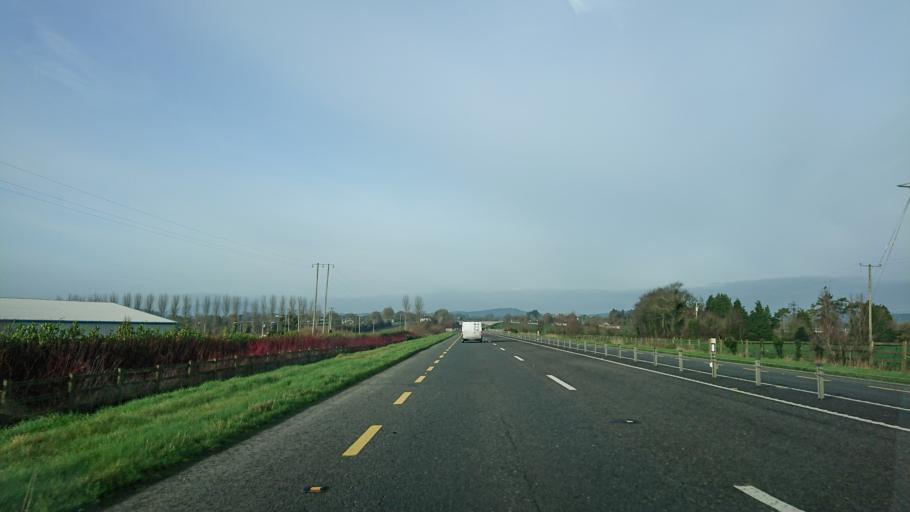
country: IE
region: Leinster
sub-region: Kilkenny
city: Piltown
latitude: 52.3421
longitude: -7.3289
